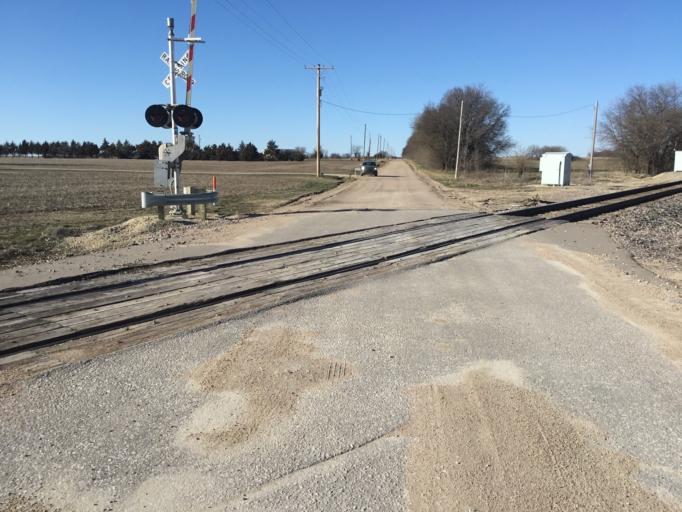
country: US
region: Kansas
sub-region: Sedgwick County
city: Kechi
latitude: 37.8140
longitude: -97.2627
